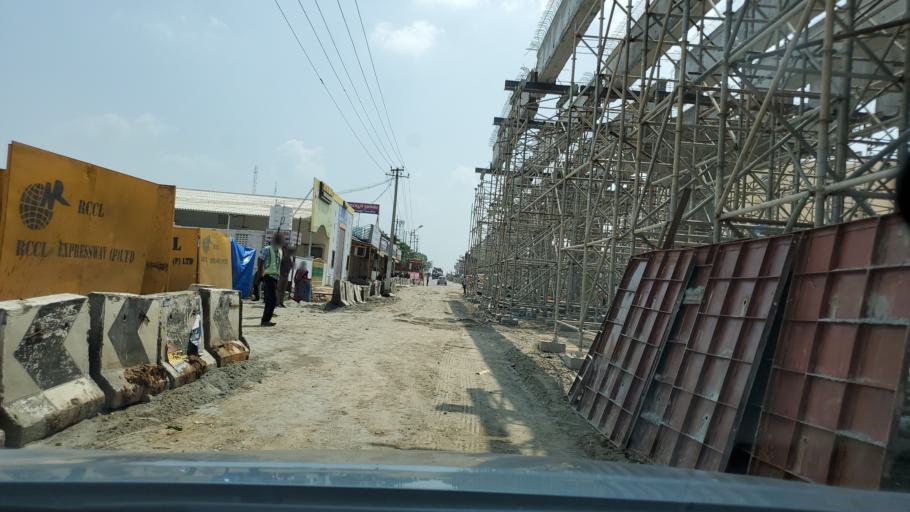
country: IN
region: Tamil Nadu
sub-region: Tiruppur
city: Dharapuram
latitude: 10.7343
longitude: 77.5180
